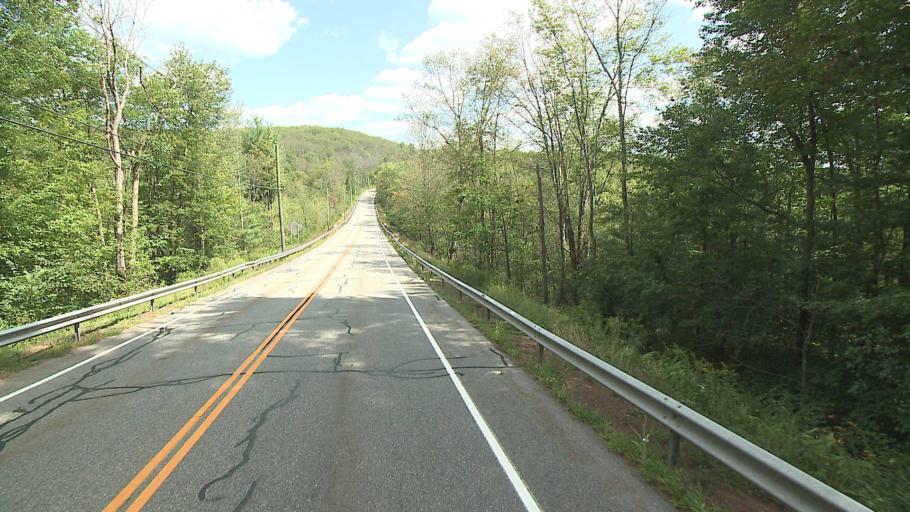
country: US
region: Connecticut
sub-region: Tolland County
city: Crystal Lake
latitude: 41.9197
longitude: -72.4110
